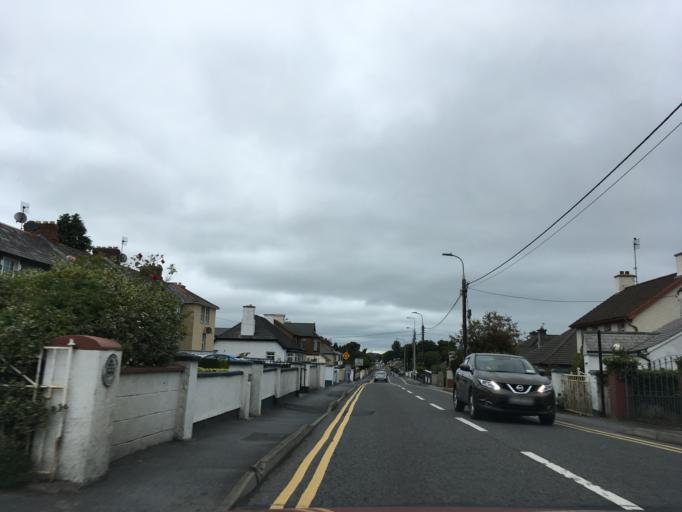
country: IE
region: Munster
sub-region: An Clar
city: Ennis
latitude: 52.8386
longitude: -8.9790
